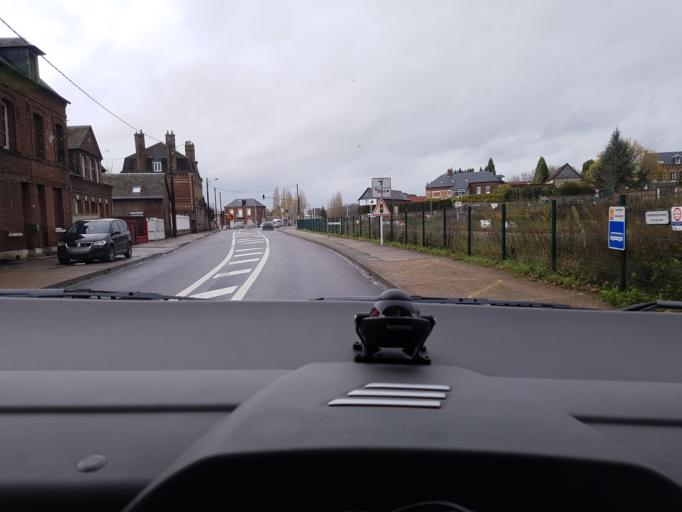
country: FR
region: Haute-Normandie
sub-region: Departement de la Seine-Maritime
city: Gournay-en-Bray
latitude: 49.4824
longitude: 1.7363
